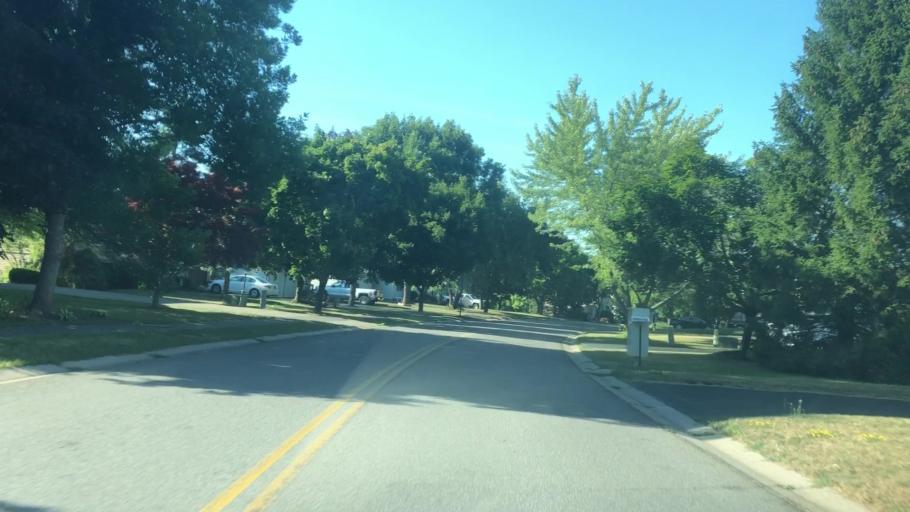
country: US
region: New York
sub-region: Wayne County
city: Macedon
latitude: 43.1258
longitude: -77.2990
